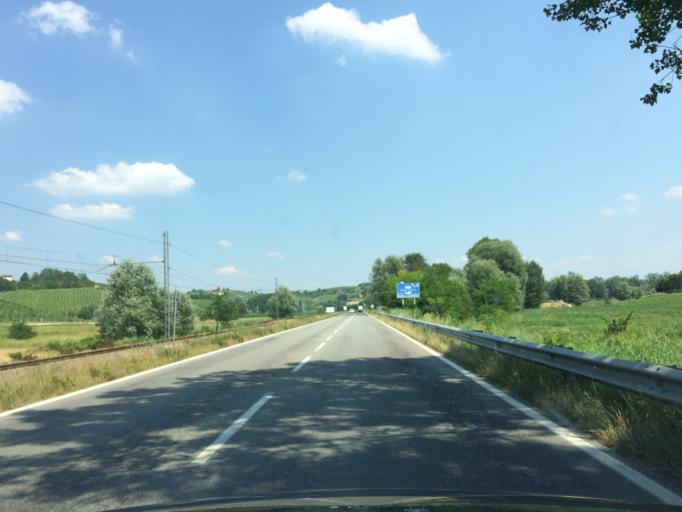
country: IT
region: Piedmont
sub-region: Provincia di Asti
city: Castelnuovo Calcea
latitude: 44.7762
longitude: 8.2905
